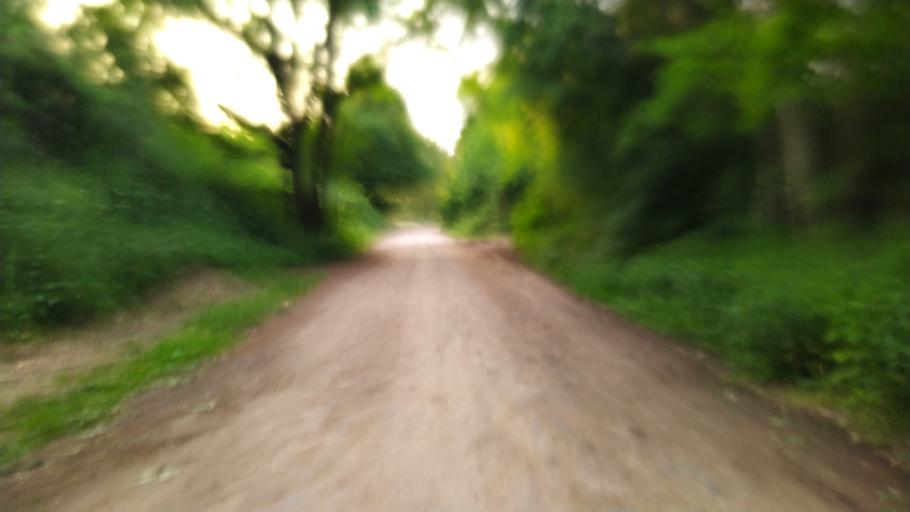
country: DE
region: Lower Saxony
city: Neu Wulmstorf
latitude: 53.4783
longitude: 9.8282
